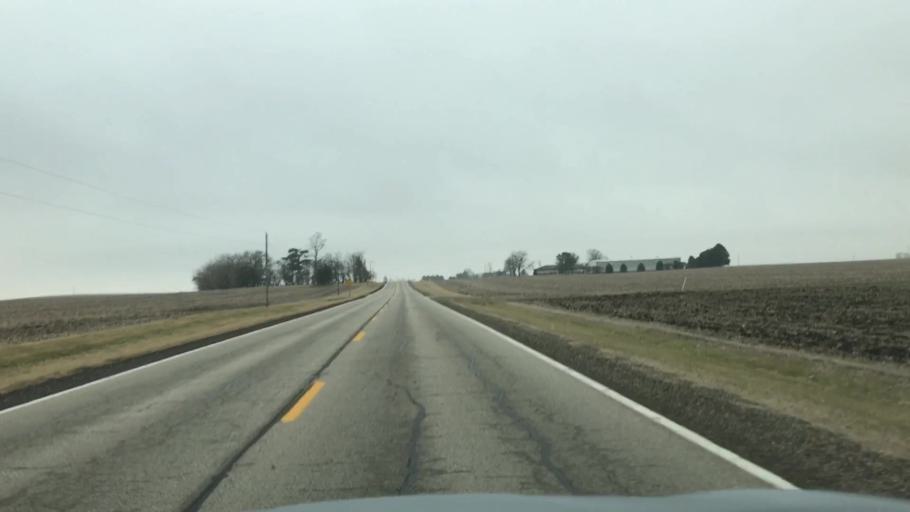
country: US
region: Illinois
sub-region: McLean County
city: Hudson
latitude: 40.5955
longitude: -88.9448
